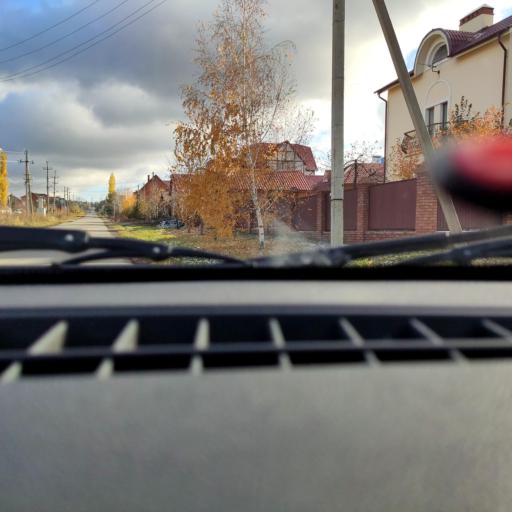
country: RU
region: Bashkortostan
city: Ufa
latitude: 54.5990
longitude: 55.9339
